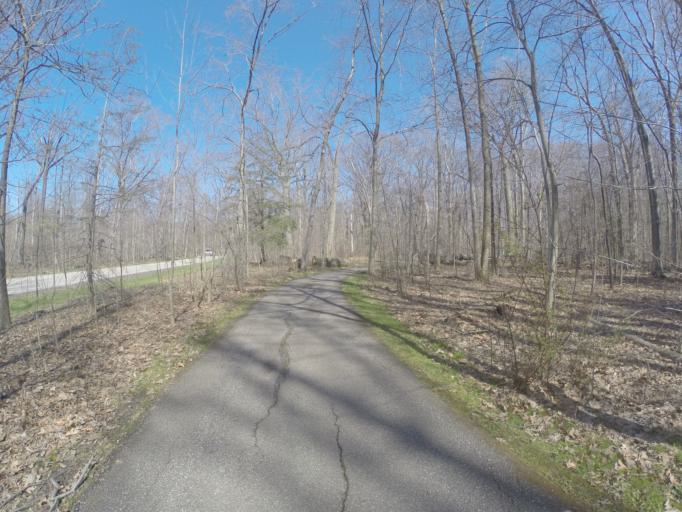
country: US
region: Ohio
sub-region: Lake County
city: Willoughby Hills
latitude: 41.5786
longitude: -81.4285
